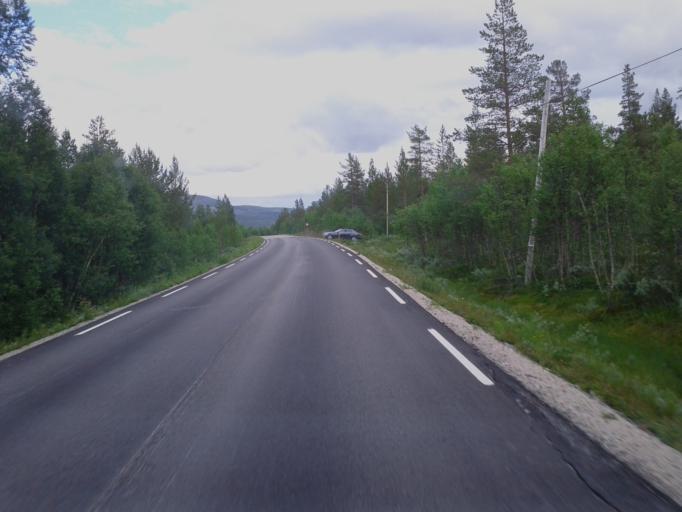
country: NO
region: Sor-Trondelag
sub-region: Roros
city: Roros
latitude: 62.3100
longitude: 11.6780
